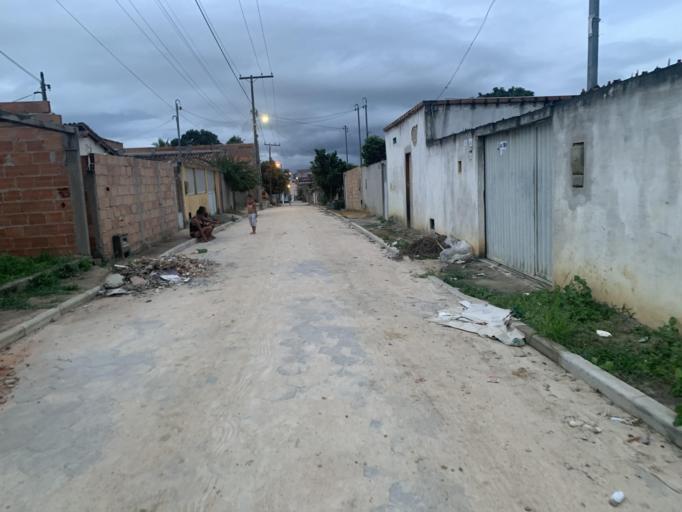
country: BR
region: Bahia
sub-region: Medeiros Neto
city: Medeiros Neto
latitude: -17.3903
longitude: -40.2332
